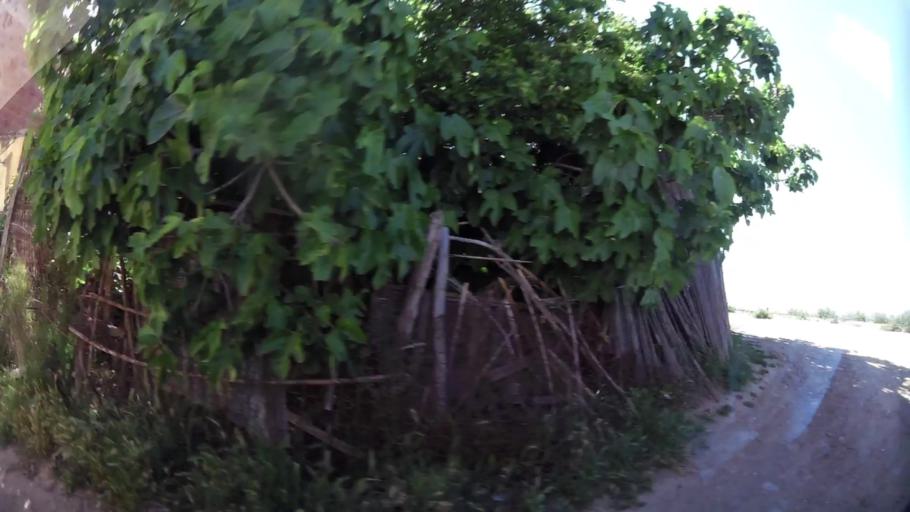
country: MA
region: Oriental
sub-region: Oujda-Angad
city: Oujda
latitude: 34.6917
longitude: -1.9269
